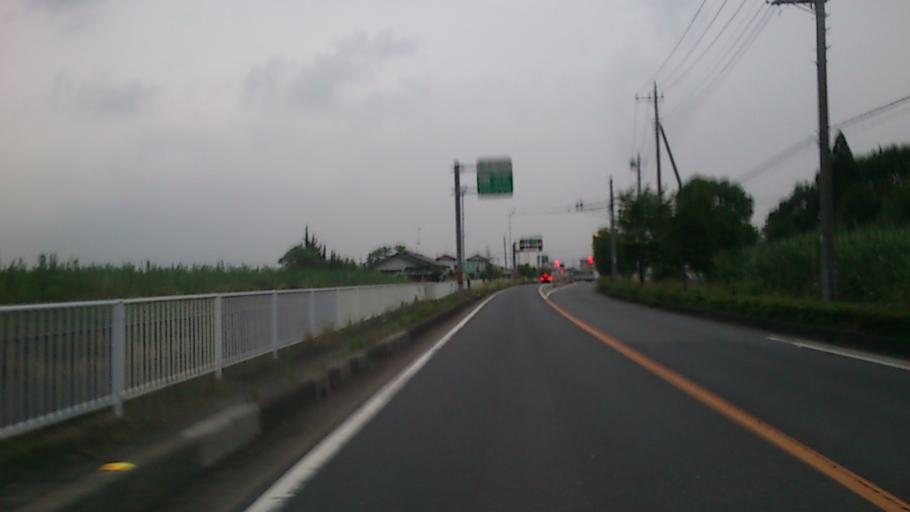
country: JP
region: Saitama
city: Kazo
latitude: 36.1654
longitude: 139.5866
